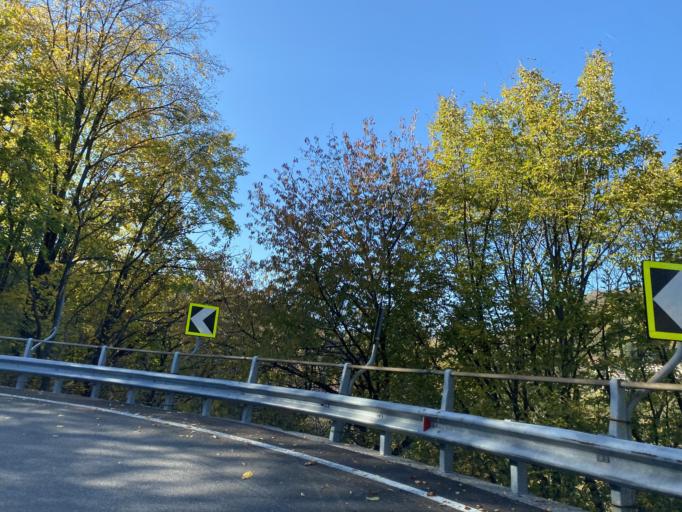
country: IT
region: Lombardy
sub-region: Provincia di Como
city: Laino
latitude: 45.9879
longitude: 9.0733
